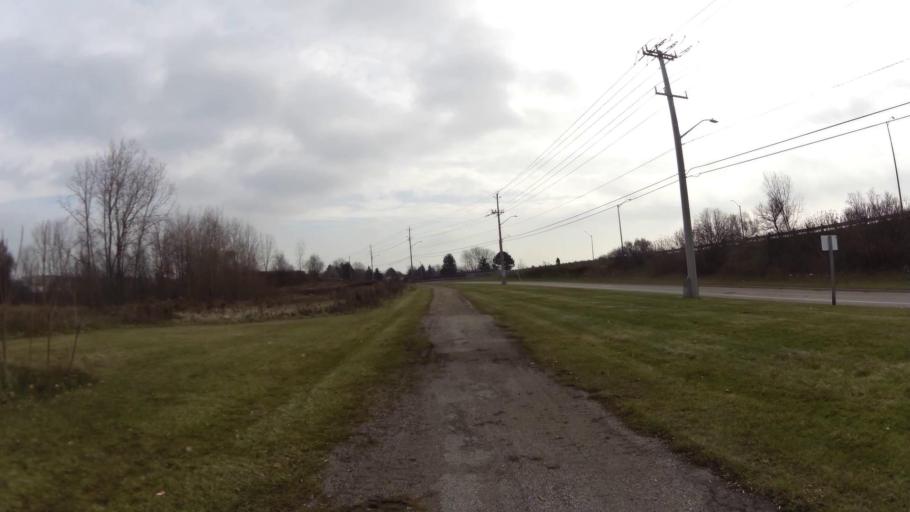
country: CA
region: Ontario
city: Kitchener
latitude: 43.3990
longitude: -80.4529
